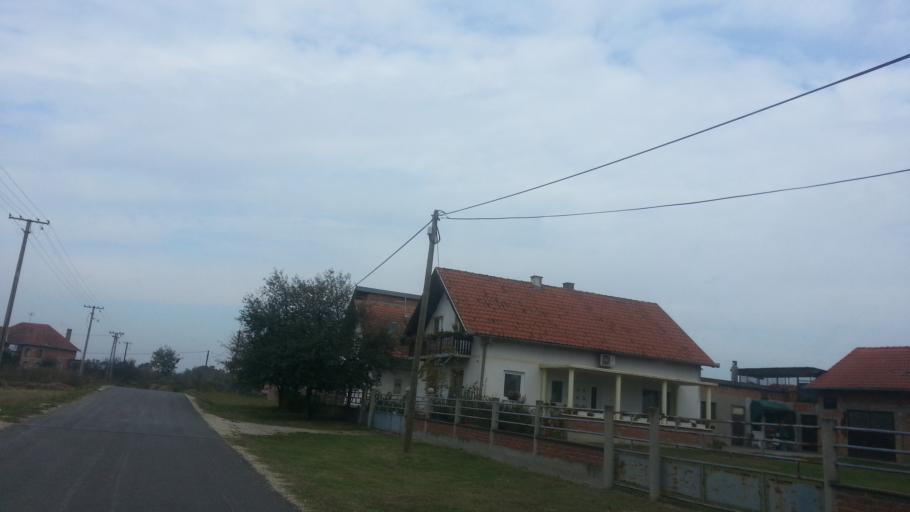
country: RS
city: Surduk
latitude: 45.0659
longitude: 20.3254
